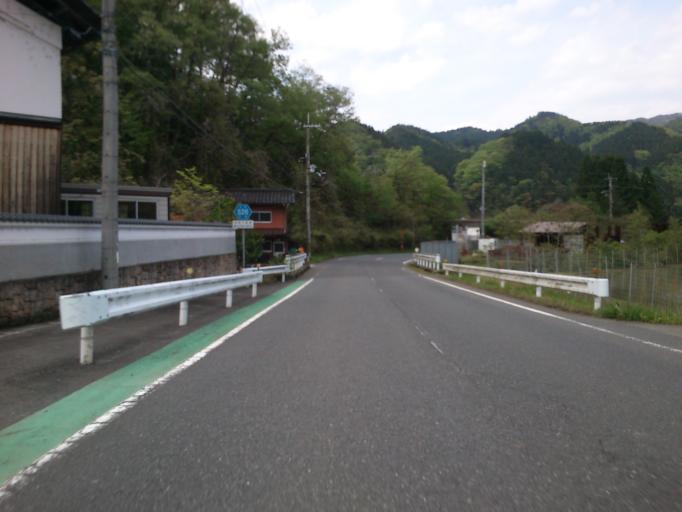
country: JP
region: Kyoto
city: Fukuchiyama
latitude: 35.3223
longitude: 134.9578
